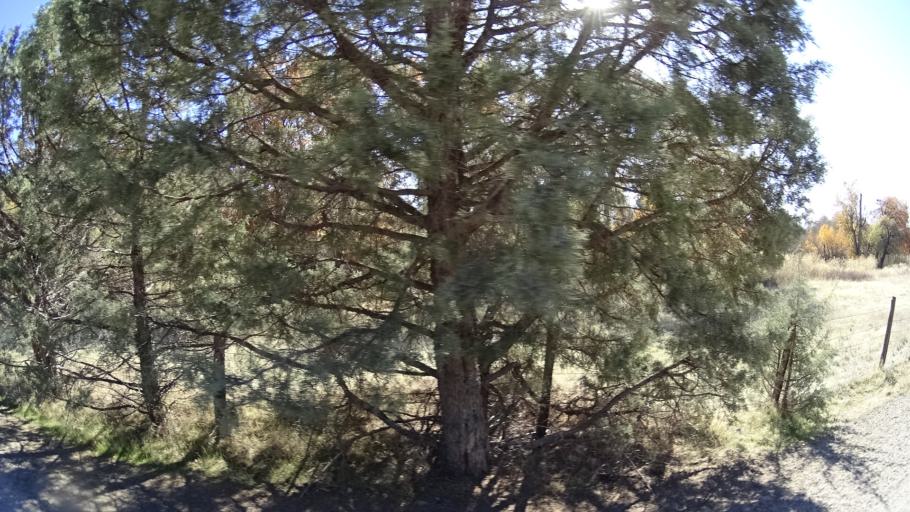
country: US
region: California
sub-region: Siskiyou County
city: Montague
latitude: 41.7330
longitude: -122.3510
